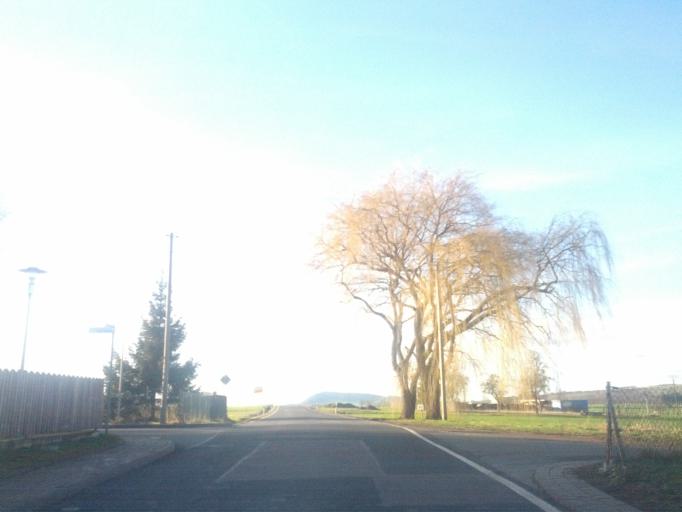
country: DE
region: Thuringia
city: Horselgau
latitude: 50.9352
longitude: 10.5700
